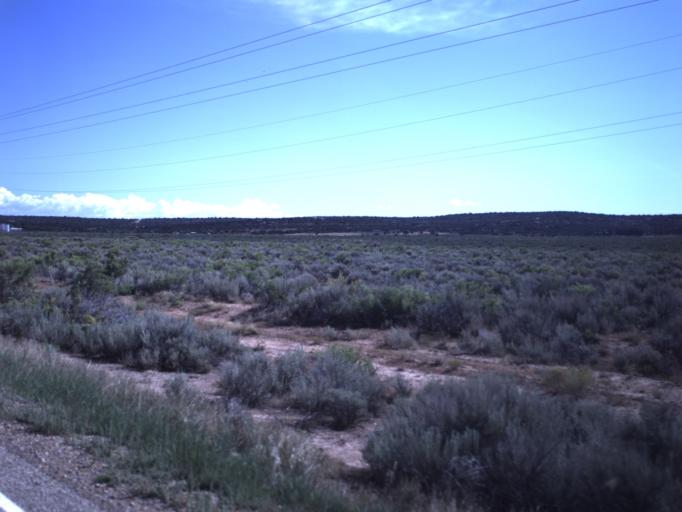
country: US
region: Utah
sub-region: Duchesne County
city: Duchesne
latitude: 40.2770
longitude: -110.3793
